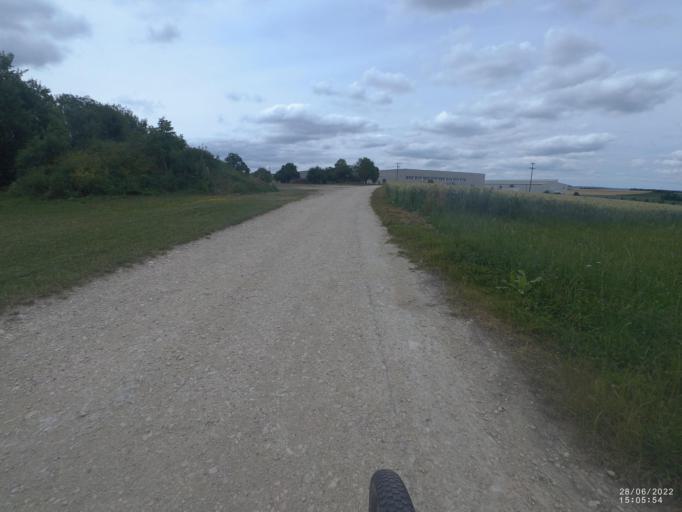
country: DE
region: Baden-Wuerttemberg
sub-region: Regierungsbezirk Stuttgart
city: Gerstetten
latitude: 48.6271
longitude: 10.0143
